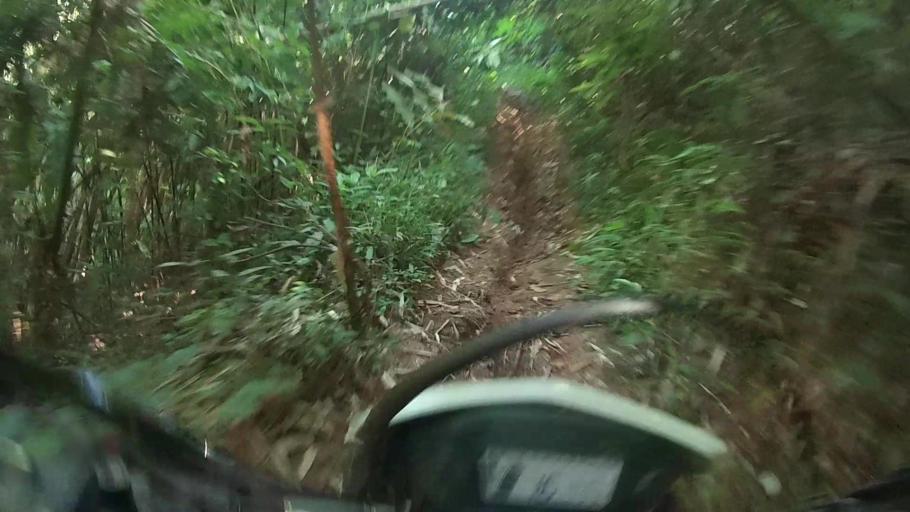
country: TH
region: Chiang Mai
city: Phrao
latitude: 19.4688
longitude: 99.2508
